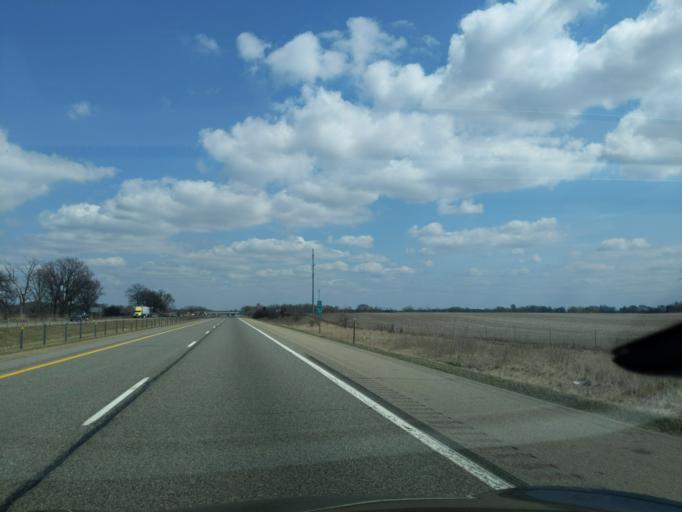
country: US
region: Michigan
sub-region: Calhoun County
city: Marshall
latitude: 42.2972
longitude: -85.0179
